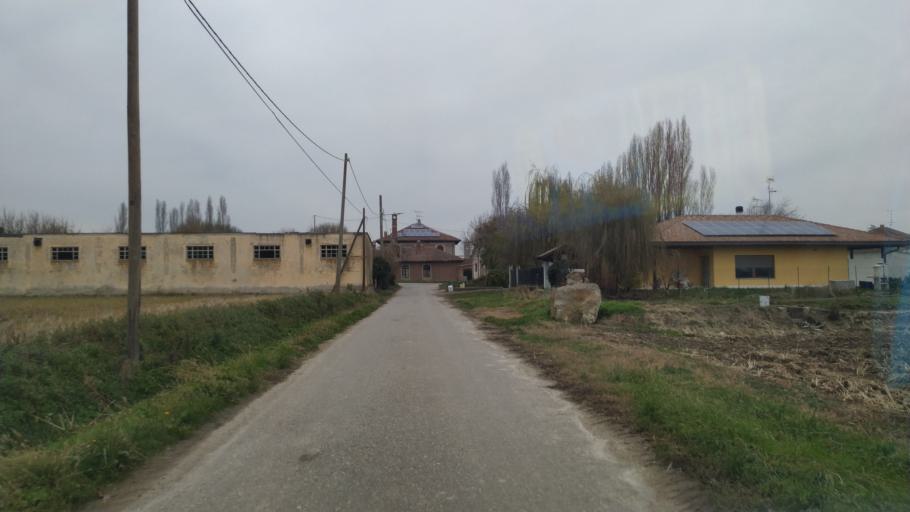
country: IT
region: Piedmont
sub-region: Provincia di Vercelli
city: Sali Vercellese
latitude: 45.3074
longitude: 8.3265
